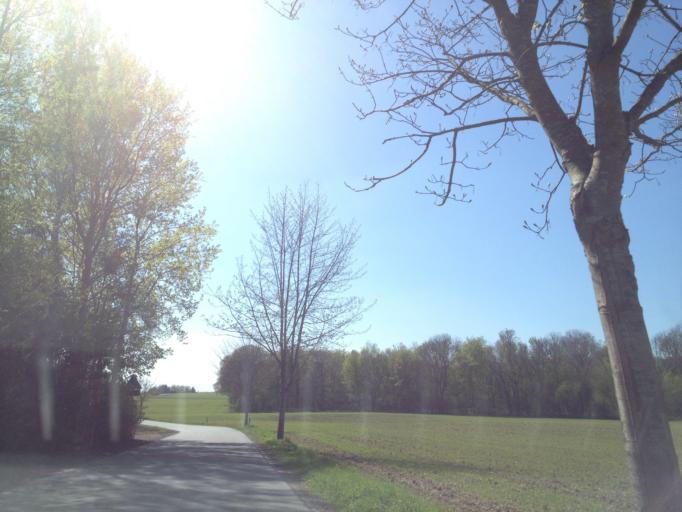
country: DK
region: Zealand
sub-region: Roskilde Kommune
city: Viby
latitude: 55.5187
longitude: 12.0168
